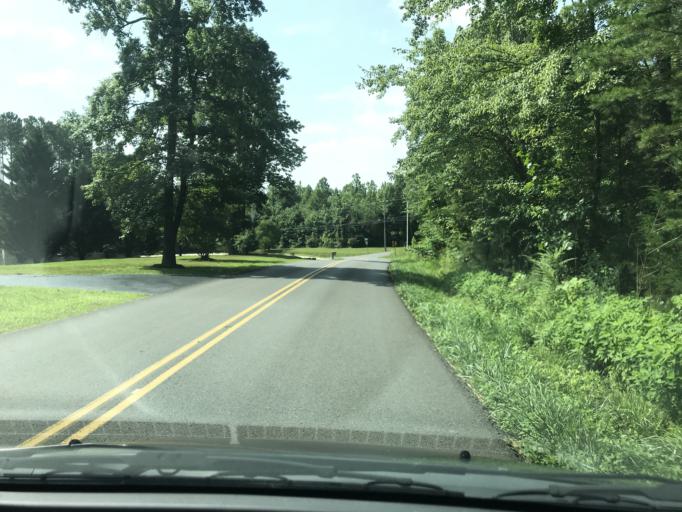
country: US
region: Tennessee
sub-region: Hamilton County
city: Apison
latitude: 35.0750
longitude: -84.9928
